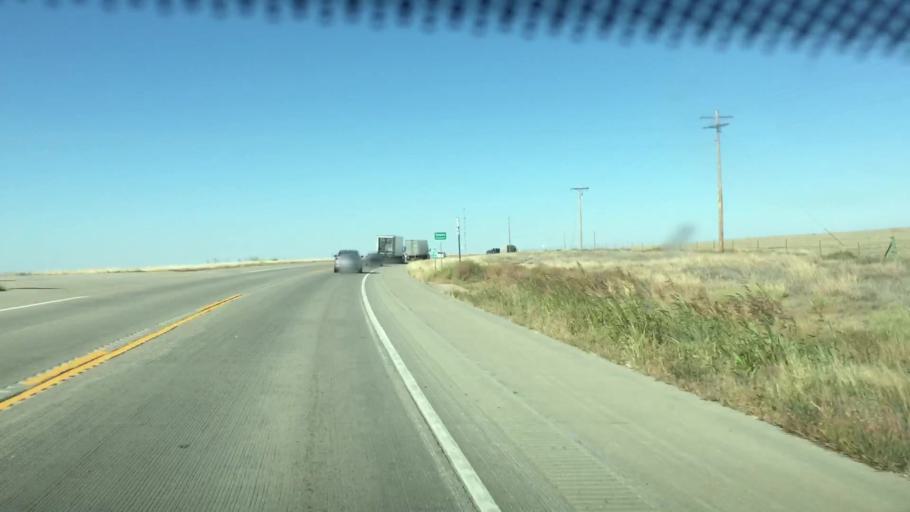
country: US
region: Colorado
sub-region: Prowers County
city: Lamar
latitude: 38.2670
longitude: -102.7237
